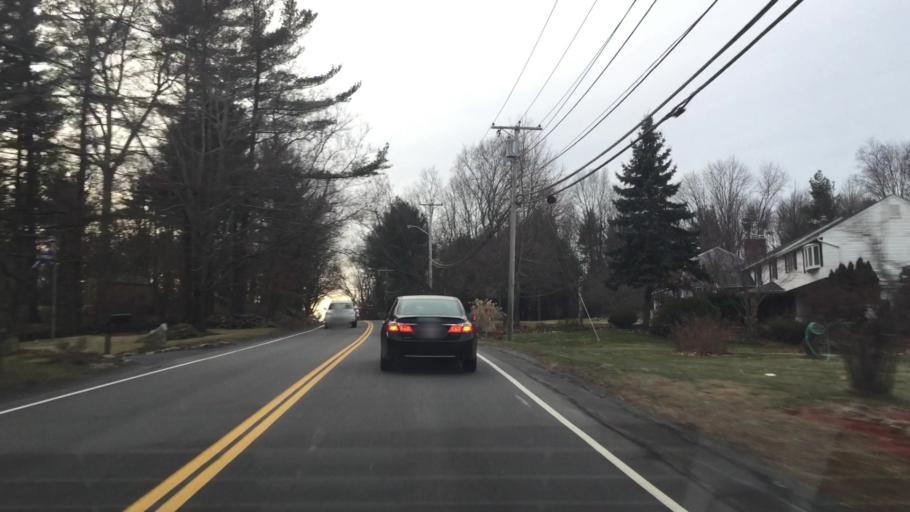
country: US
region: New Hampshire
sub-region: Rockingham County
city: Windham
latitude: 42.7598
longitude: -71.2604
